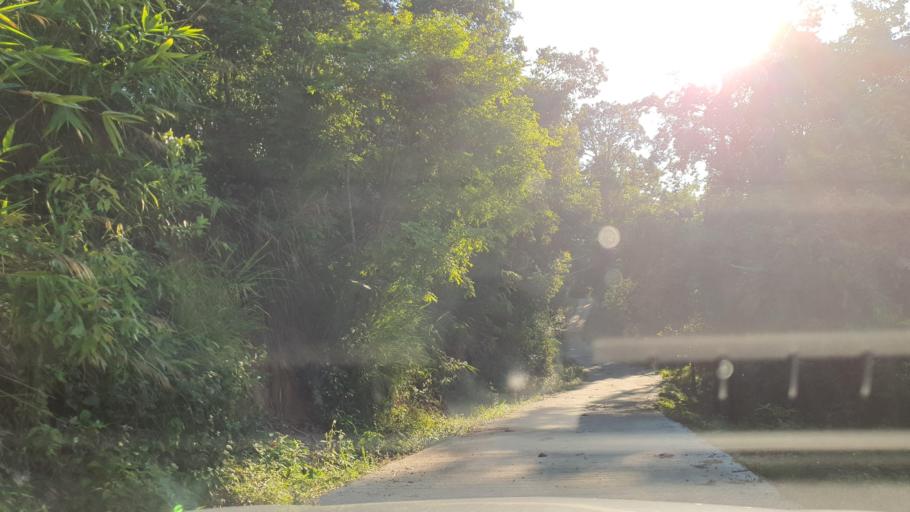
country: TH
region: Chiang Mai
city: Mae On
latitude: 18.8132
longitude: 99.3183
